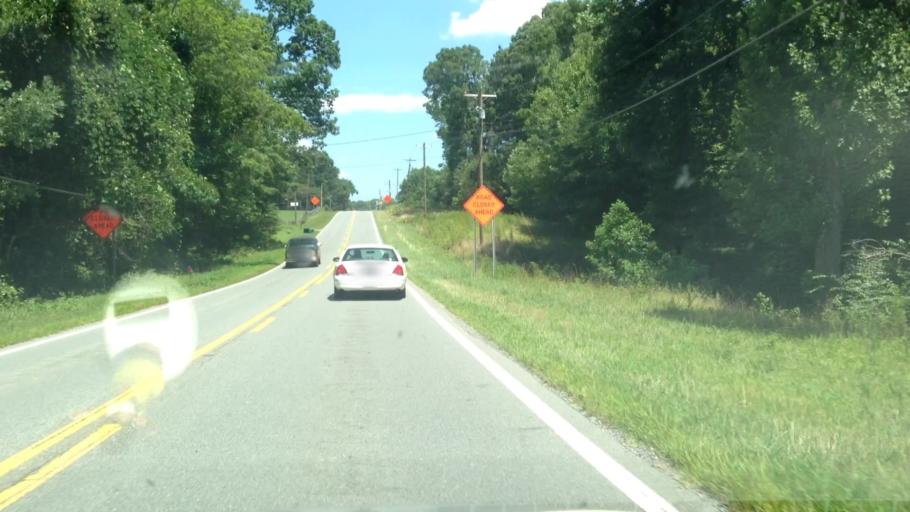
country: US
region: North Carolina
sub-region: Rockingham County
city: Reidsville
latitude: 36.3333
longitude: -79.7012
